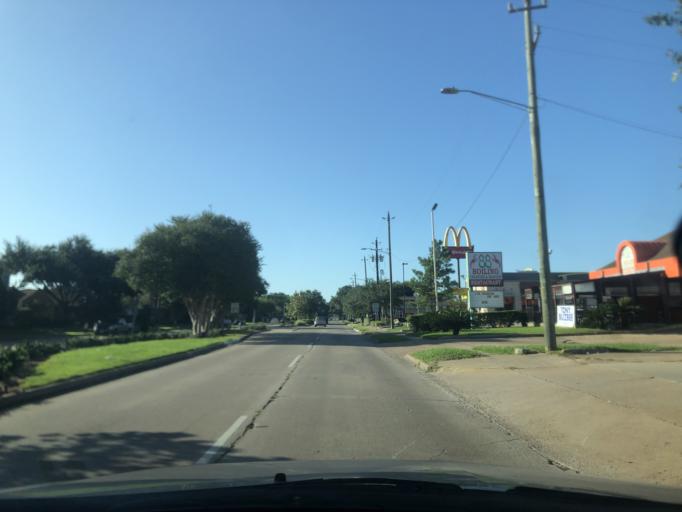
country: US
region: Texas
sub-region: Harris County
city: Bunker Hill Village
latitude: 29.7476
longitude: -95.5722
